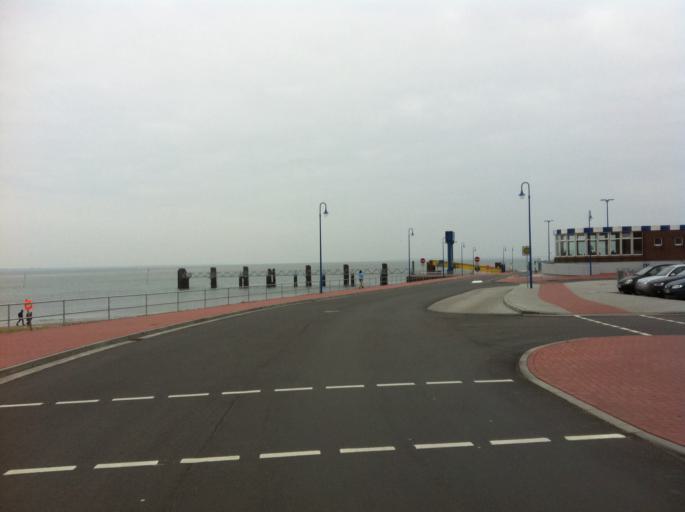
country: DE
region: Schleswig-Holstein
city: Wittdun
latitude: 54.6273
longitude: 8.3962
